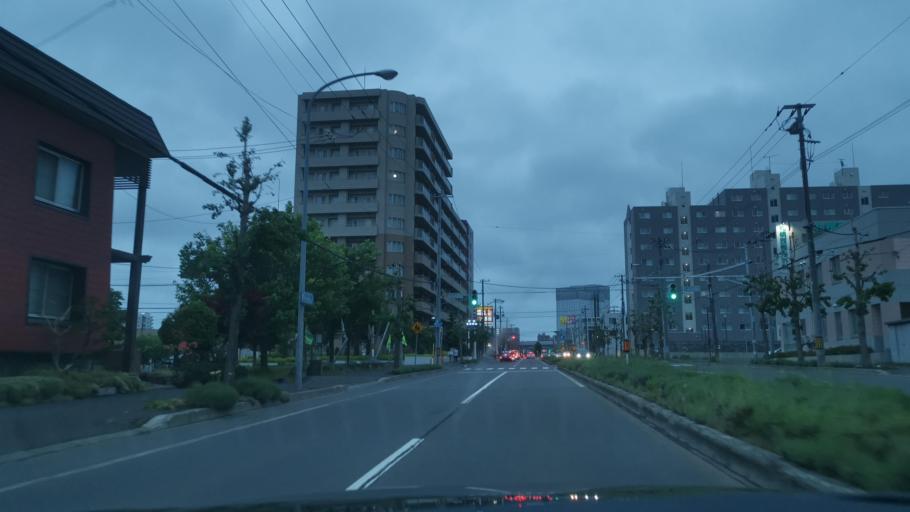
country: JP
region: Hokkaido
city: Sapporo
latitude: 43.0944
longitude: 141.2697
